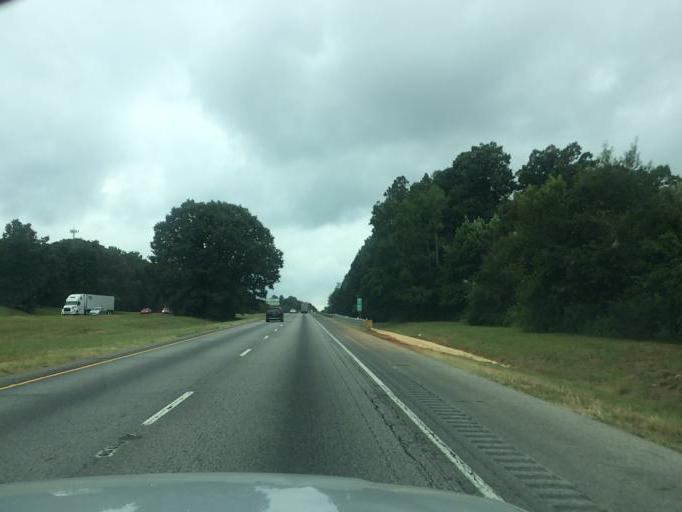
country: US
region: Georgia
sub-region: Franklin County
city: Carnesville
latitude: 34.3545
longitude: -83.3036
